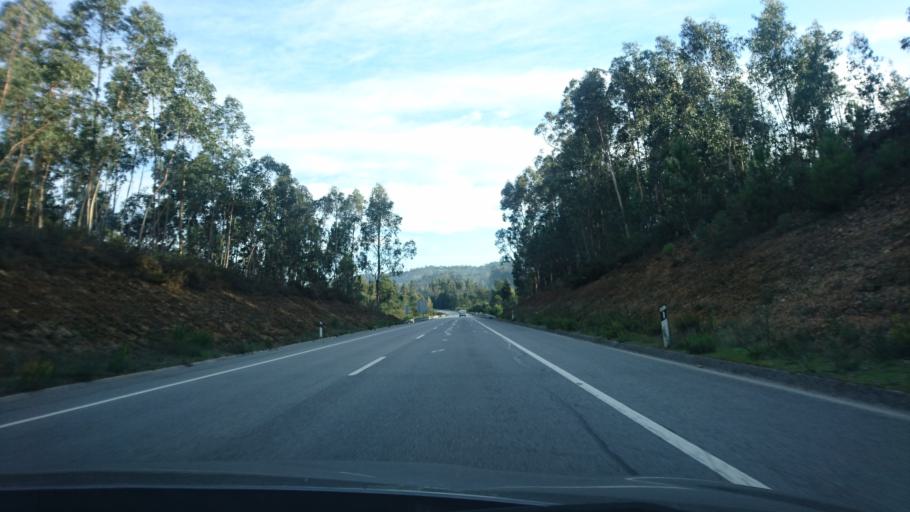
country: PT
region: Aveiro
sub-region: Santa Maria da Feira
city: Milheiros de Poiares
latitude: 40.9296
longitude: -8.4822
